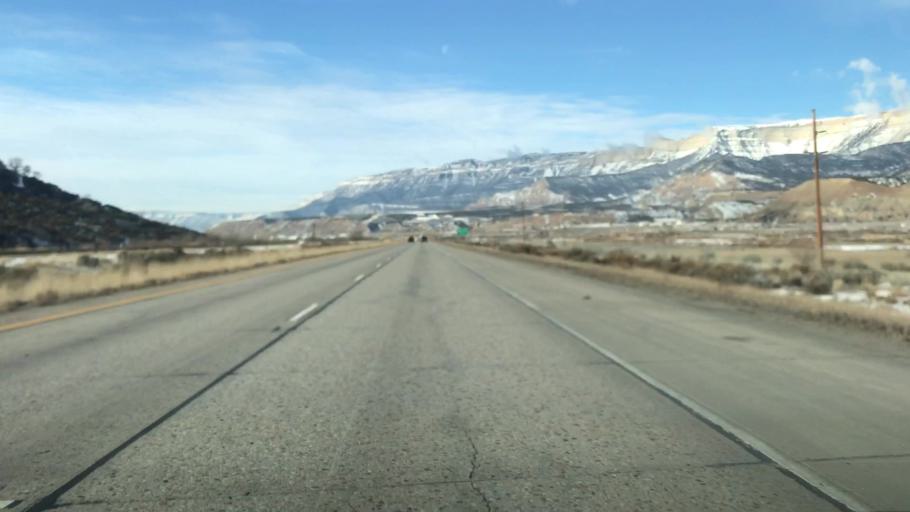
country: US
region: Colorado
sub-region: Garfield County
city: Rifle
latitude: 39.5204
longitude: -107.8190
